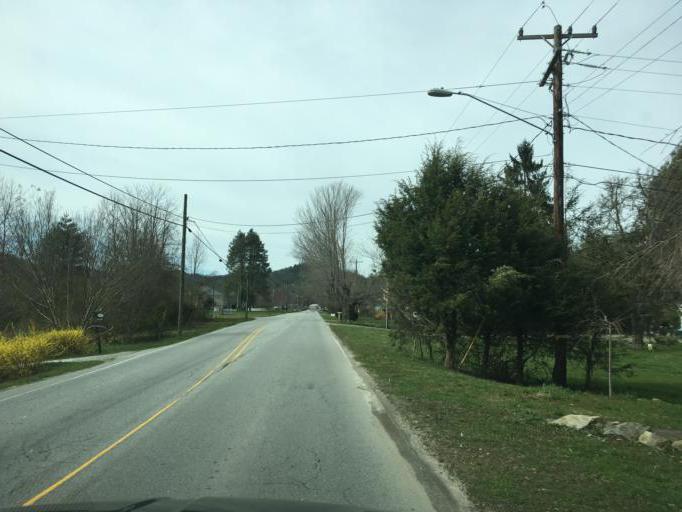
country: US
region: North Carolina
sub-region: Transylvania County
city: Brevard
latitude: 35.2564
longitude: -82.7019
